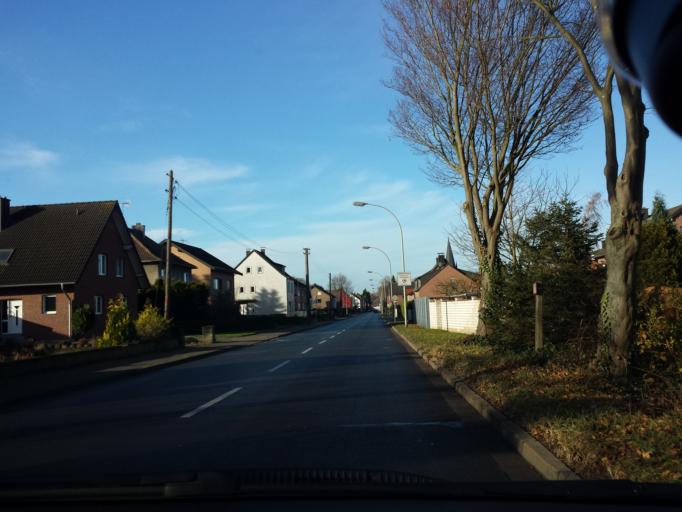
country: DE
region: North Rhine-Westphalia
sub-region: Regierungsbezirk Koln
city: Ubach-Palenberg
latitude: 50.9270
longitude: 6.0746
